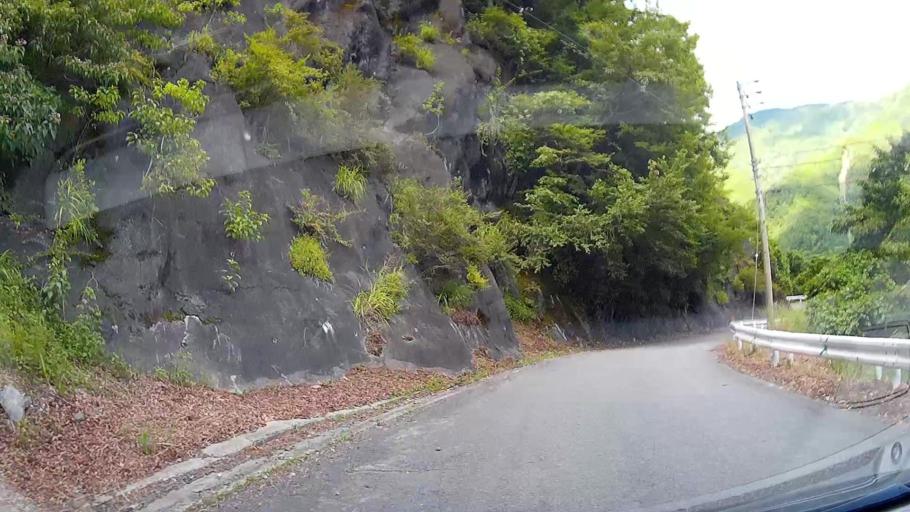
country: JP
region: Shizuoka
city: Shizuoka-shi
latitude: 35.2908
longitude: 138.2173
